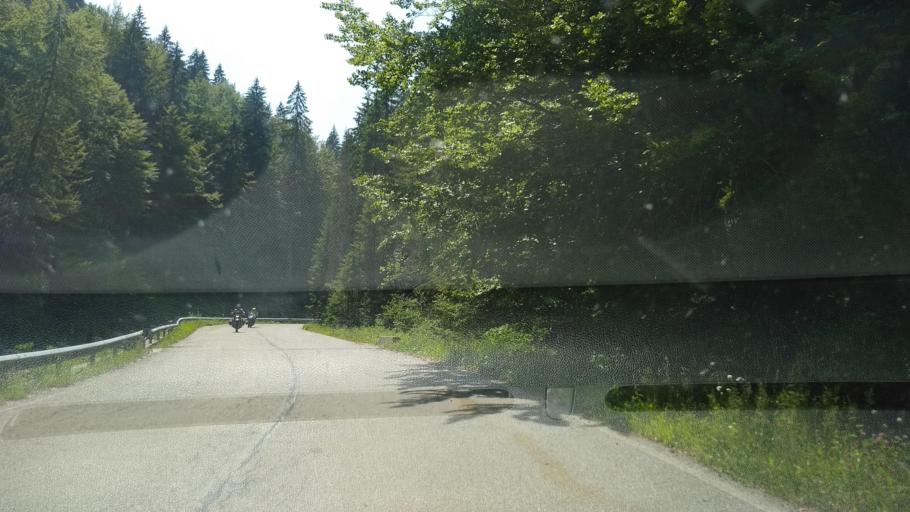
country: RO
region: Gorj
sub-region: Comuna Tismana
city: Sohodol
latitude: 45.2696
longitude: 22.8887
